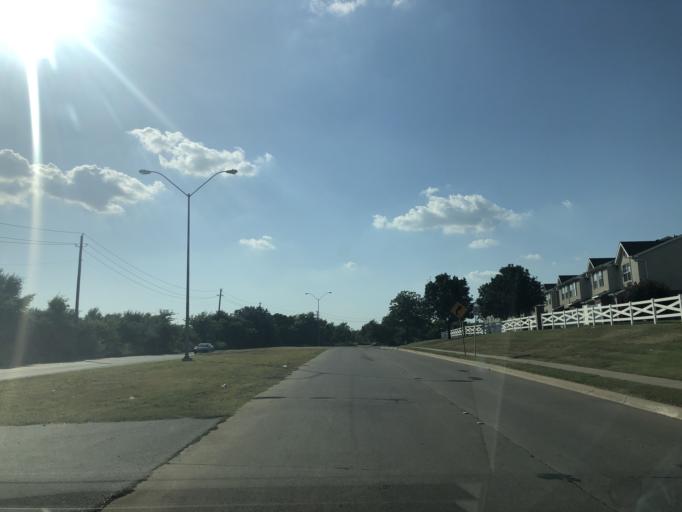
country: US
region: Texas
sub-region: Tarrant County
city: Sansom Park
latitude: 32.8182
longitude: -97.3820
